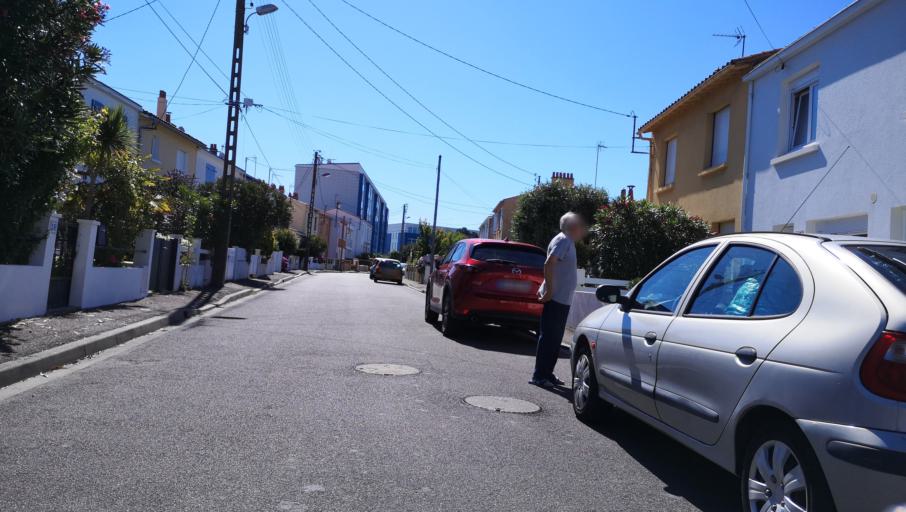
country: FR
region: Pays de la Loire
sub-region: Departement de la Vendee
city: Les Sables-d'Olonne
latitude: 46.5069
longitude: -1.7797
